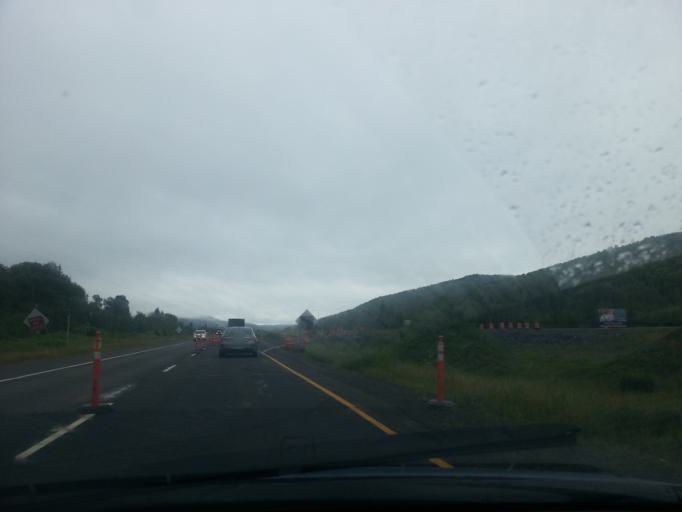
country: CA
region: Quebec
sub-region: Bas-Saint-Laurent
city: Cabano
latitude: 47.5720
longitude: -68.7073
